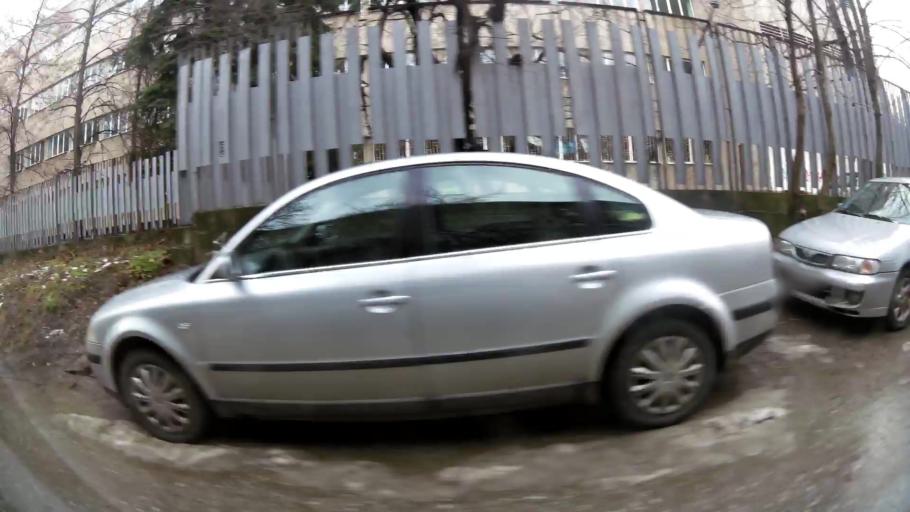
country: BG
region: Sofia-Capital
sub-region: Stolichna Obshtina
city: Sofia
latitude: 42.6664
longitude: 23.2529
